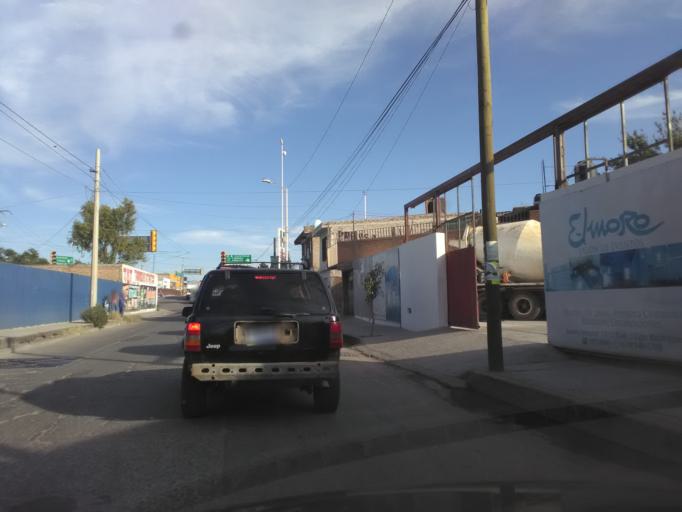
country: MX
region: Durango
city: Victoria de Durango
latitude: 24.0222
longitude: -104.6256
